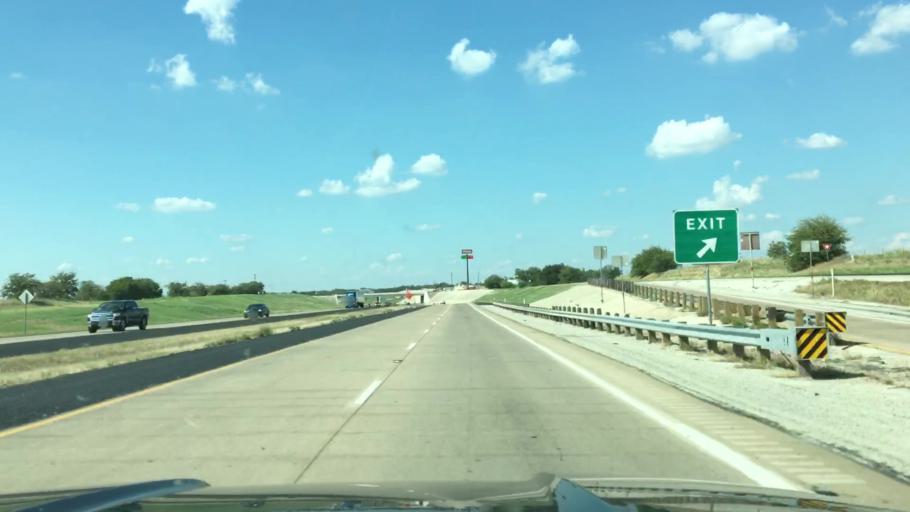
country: US
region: Texas
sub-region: Wise County
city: New Fairview
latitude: 33.0949
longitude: -97.4712
